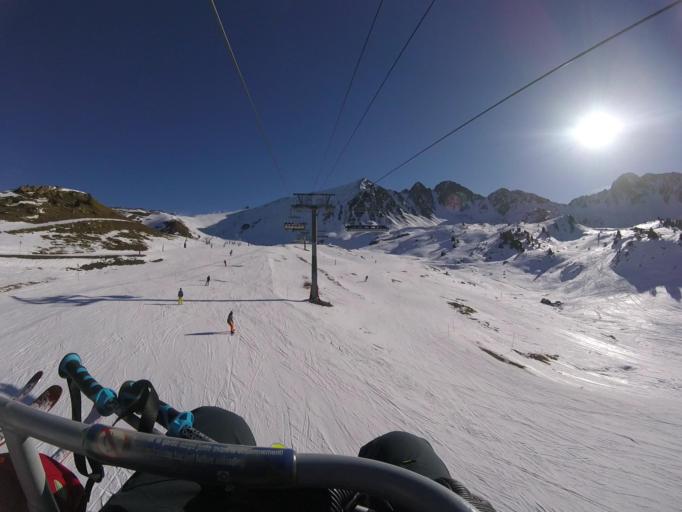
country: AD
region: Encamp
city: Pas de la Casa
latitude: 42.5269
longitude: 1.7094
